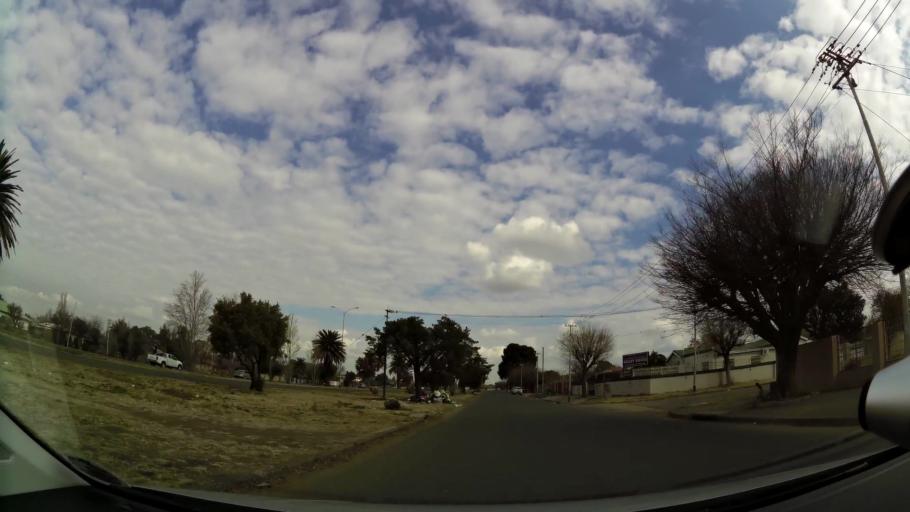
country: ZA
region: Orange Free State
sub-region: Mangaung Metropolitan Municipality
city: Bloemfontein
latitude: -29.0871
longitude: 26.2548
